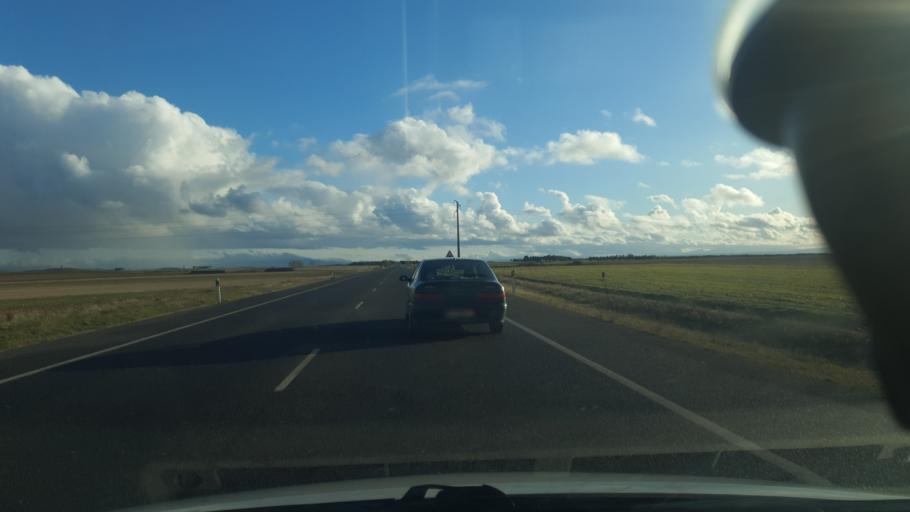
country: ES
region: Castille and Leon
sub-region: Provincia de Segovia
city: Rapariegos
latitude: 41.0869
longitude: -4.6367
